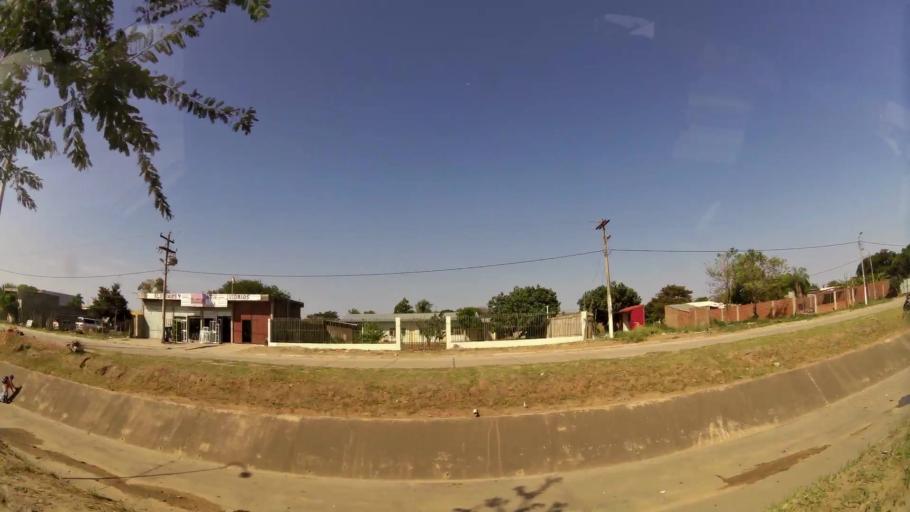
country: BO
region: Santa Cruz
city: Cotoca
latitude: -17.8054
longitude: -63.1093
